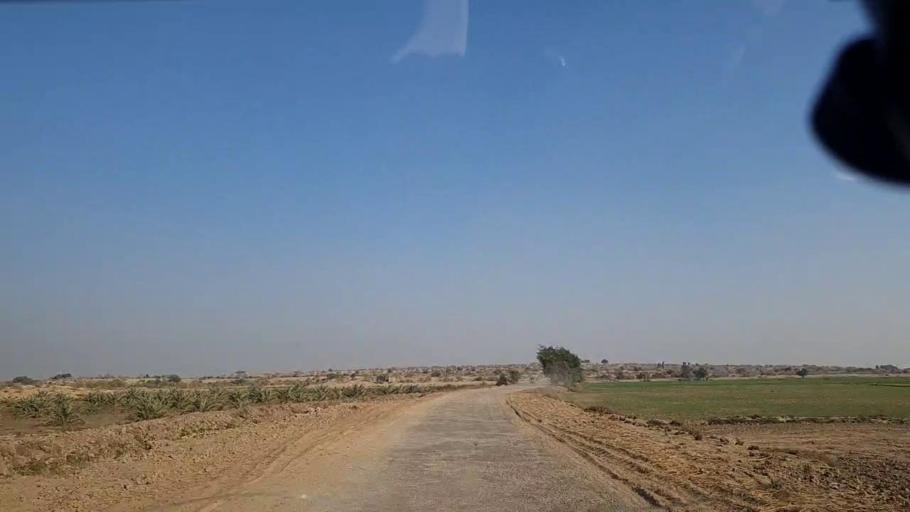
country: PK
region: Sindh
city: Khanpur
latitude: 27.6788
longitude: 69.5641
